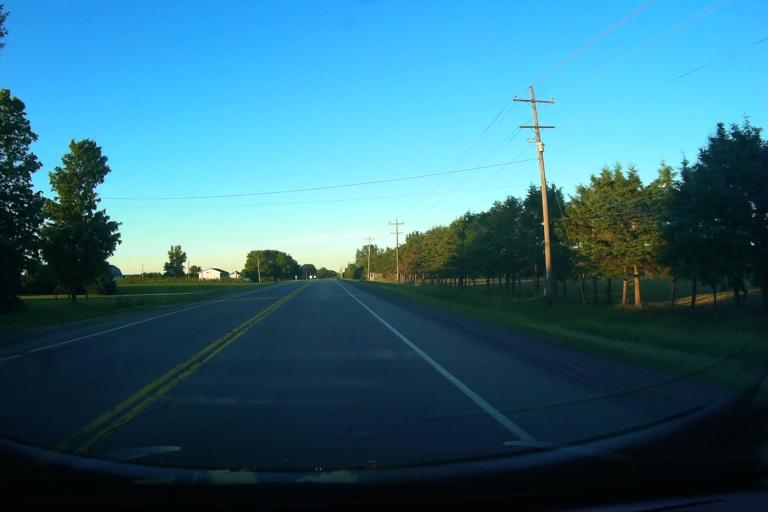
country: CA
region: Ontario
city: Casselman
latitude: 45.0753
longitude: -75.3269
